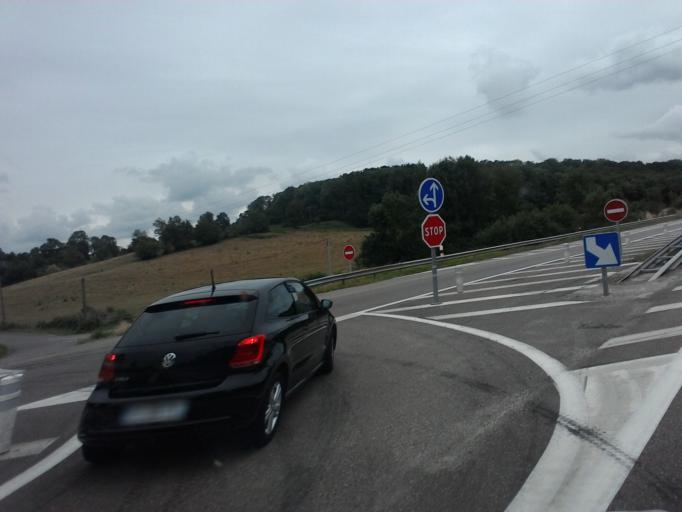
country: FR
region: Franche-Comte
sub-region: Departement du Jura
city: Lons-le-Saunier
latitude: 46.7190
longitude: 5.5567
